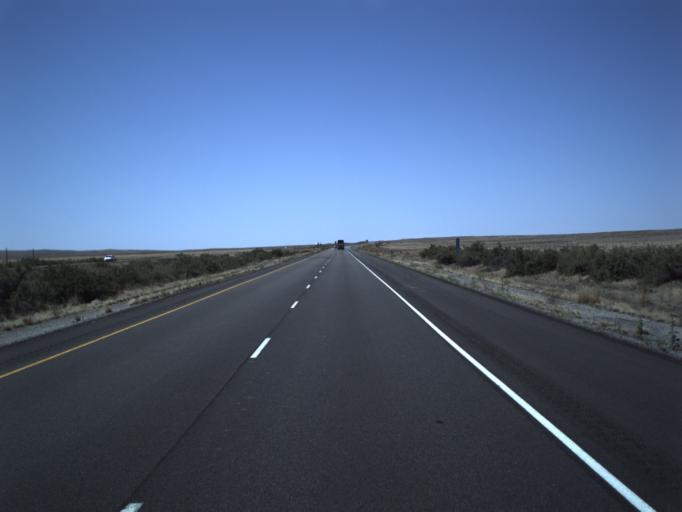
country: US
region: Colorado
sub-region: Mesa County
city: Loma
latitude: 39.0747
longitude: -109.2347
